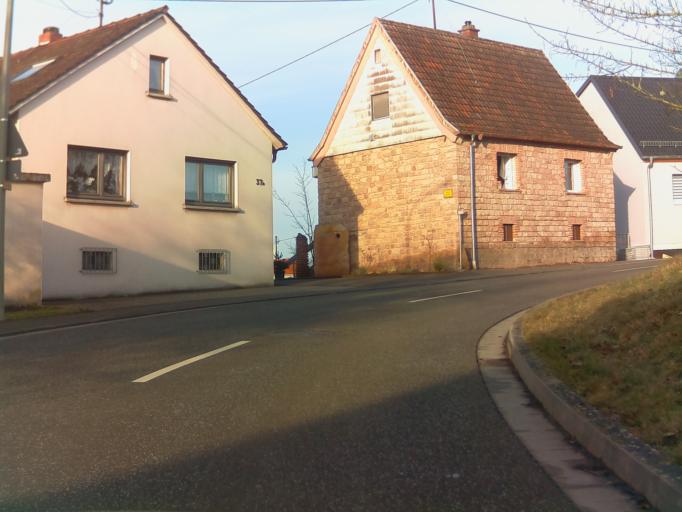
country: DE
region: Rheinland-Pfalz
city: Gries
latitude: 49.4160
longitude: 7.4088
